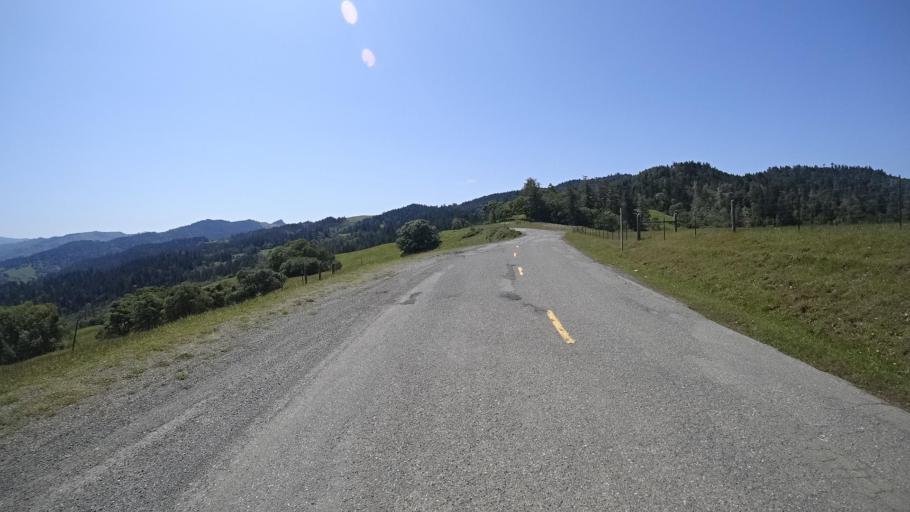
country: US
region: California
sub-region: Humboldt County
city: Redway
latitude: 40.1555
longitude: -123.6222
